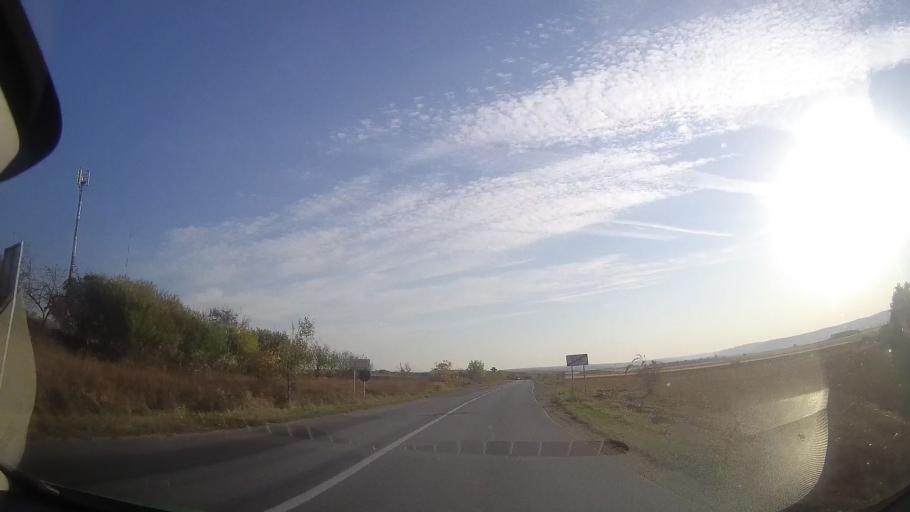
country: RO
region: Timis
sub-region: Comuna Fibis
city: Fibis
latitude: 45.9814
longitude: 21.4290
